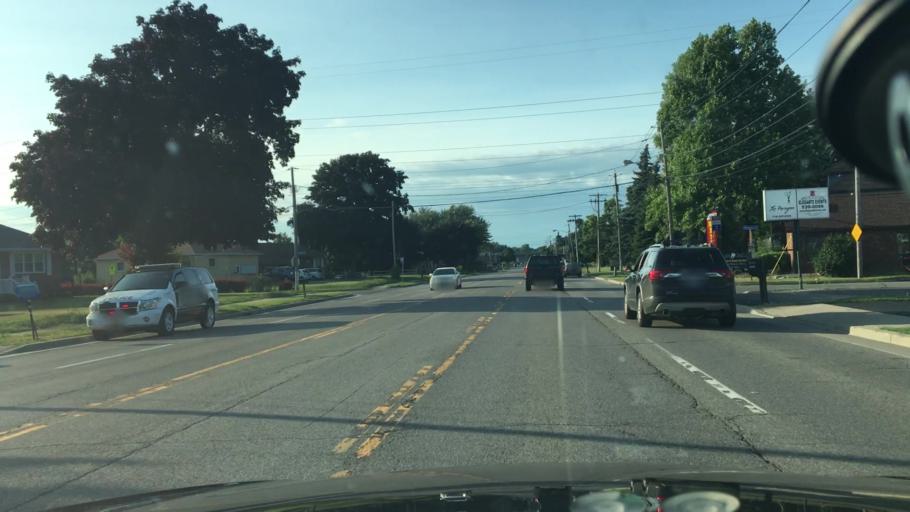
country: US
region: New York
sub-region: Erie County
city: Blasdell
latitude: 42.8058
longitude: -78.7977
